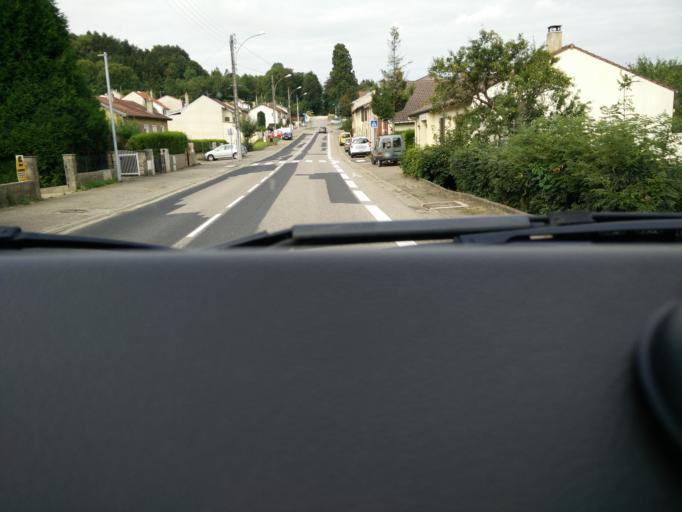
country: FR
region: Lorraine
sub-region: Departement de Meurthe-et-Moselle
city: Montauville
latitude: 48.9004
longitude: 6.0193
